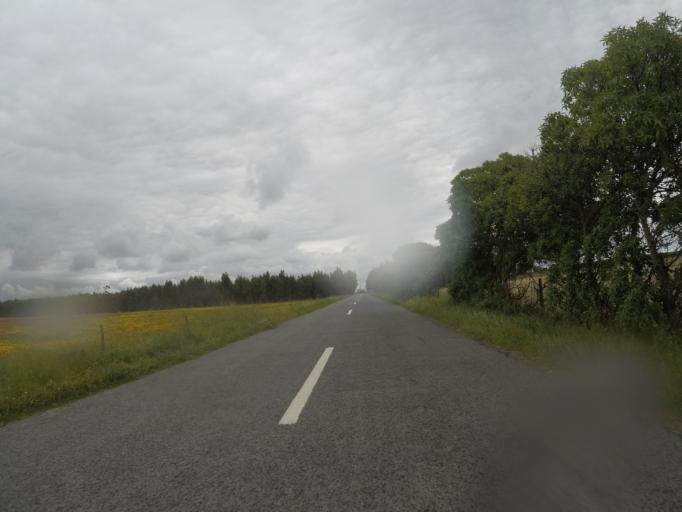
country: PT
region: Beja
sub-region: Odemira
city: Sao Teotonio
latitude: 37.5956
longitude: -8.7743
